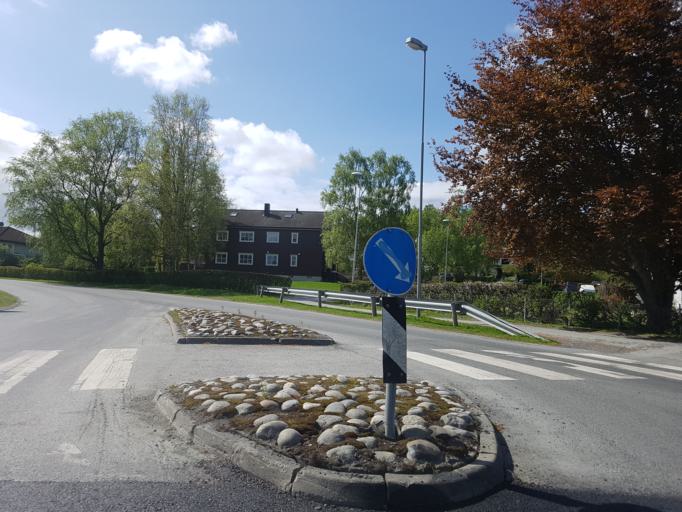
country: NO
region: Nord-Trondelag
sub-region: Levanger
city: Skogn
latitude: 63.7038
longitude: 11.1927
